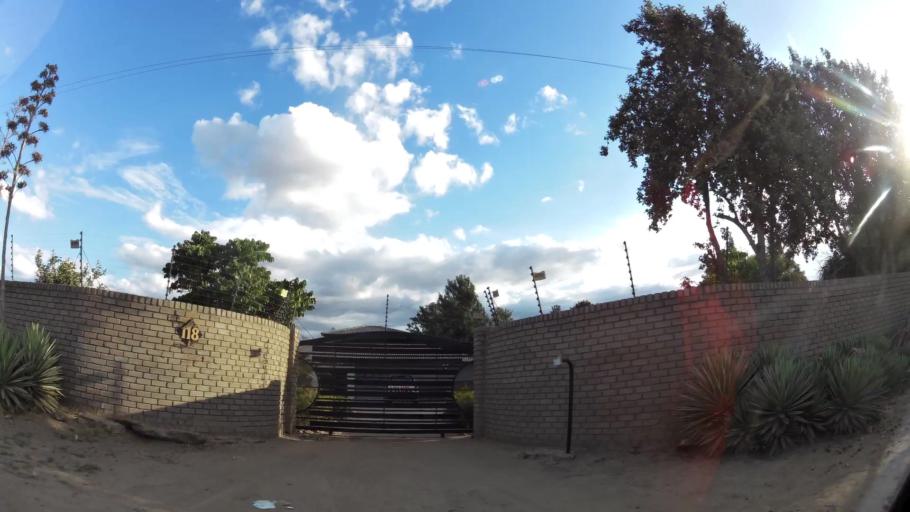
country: ZA
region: Limpopo
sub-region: Capricorn District Municipality
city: Polokwane
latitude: -23.9261
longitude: 29.4367
